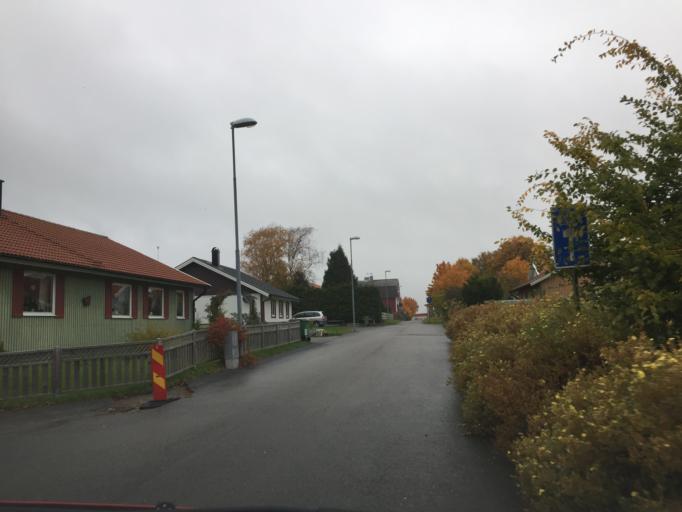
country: SE
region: Vaestra Goetaland
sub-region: Trollhattan
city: Sjuntorp
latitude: 58.1559
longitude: 12.3047
